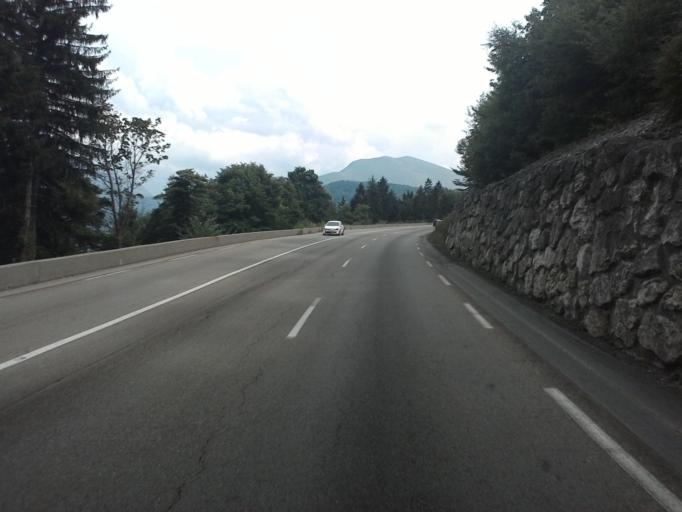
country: FR
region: Rhone-Alpes
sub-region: Departement de l'Isere
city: Notre-Dame-de-Mesage
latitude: 45.0485
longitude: 5.7561
